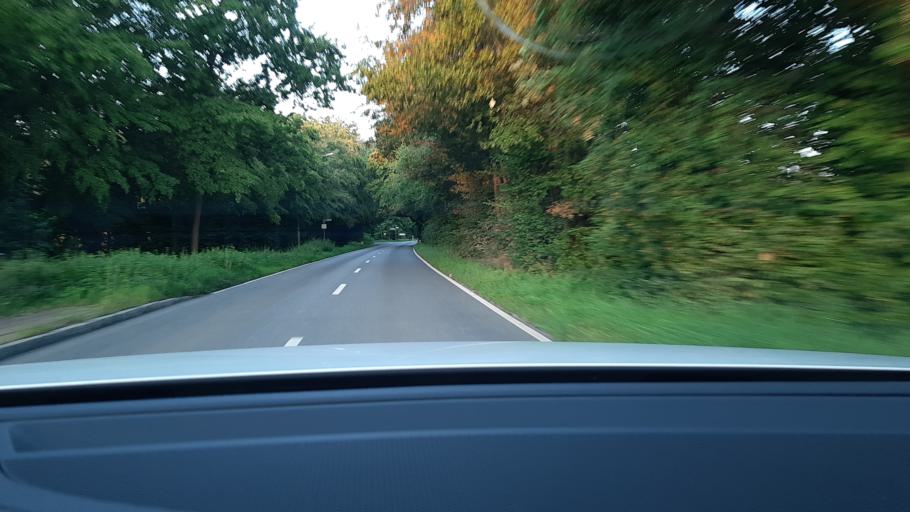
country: DE
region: Schleswig-Holstein
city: Hamberge
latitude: 53.8206
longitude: 10.5913
